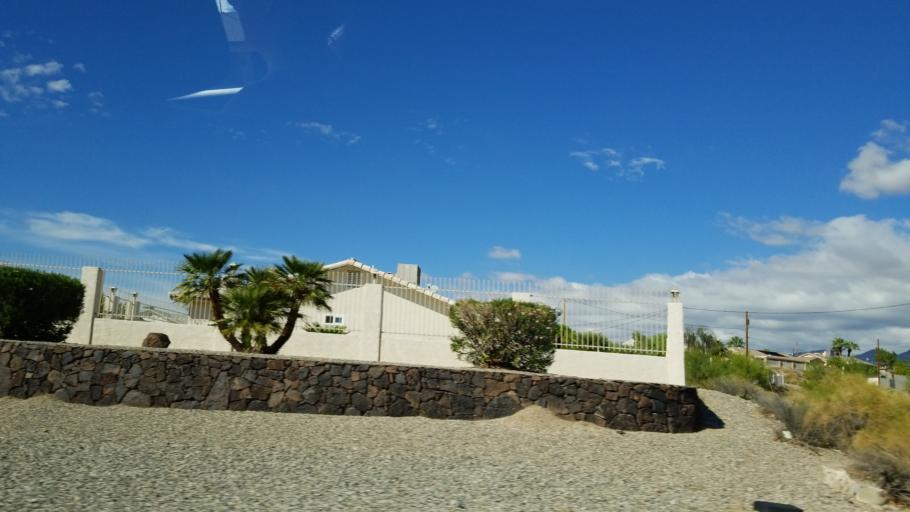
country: US
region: Arizona
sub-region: Mohave County
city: Lake Havasu City
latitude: 34.4998
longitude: -114.2801
